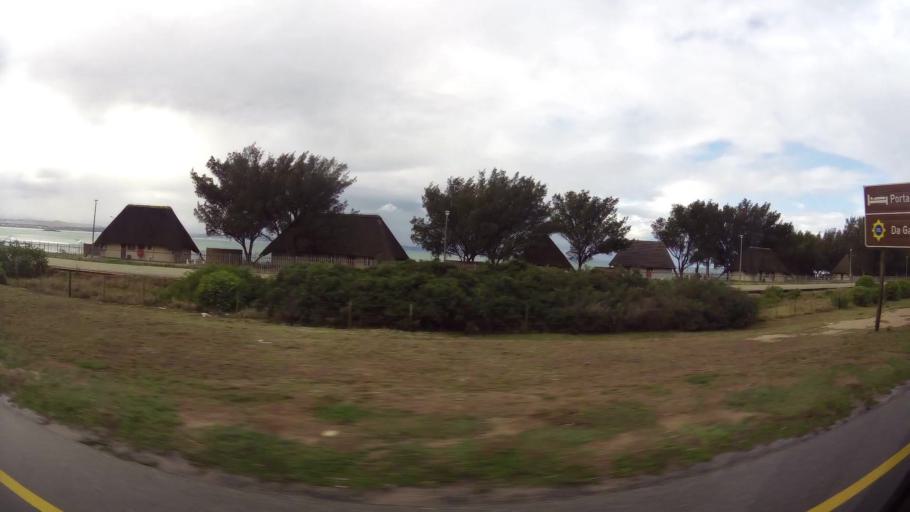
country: ZA
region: Western Cape
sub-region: Eden District Municipality
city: Mossel Bay
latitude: -34.1710
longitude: 22.1231
